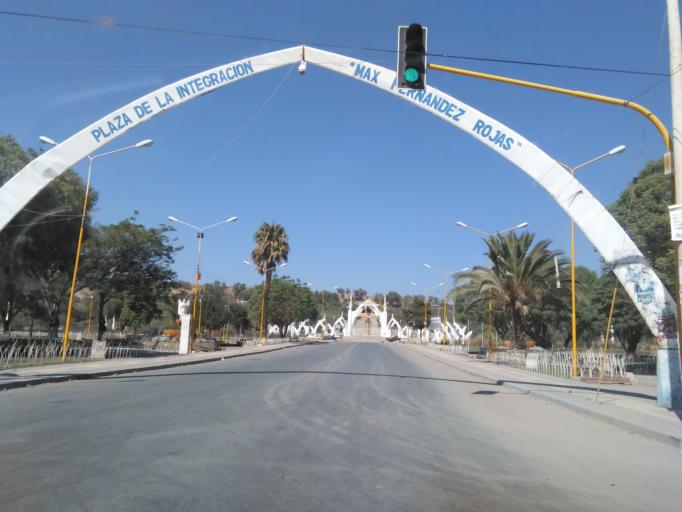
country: BO
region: Cochabamba
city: Sipe Sipe
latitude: -17.4185
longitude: -66.2835
